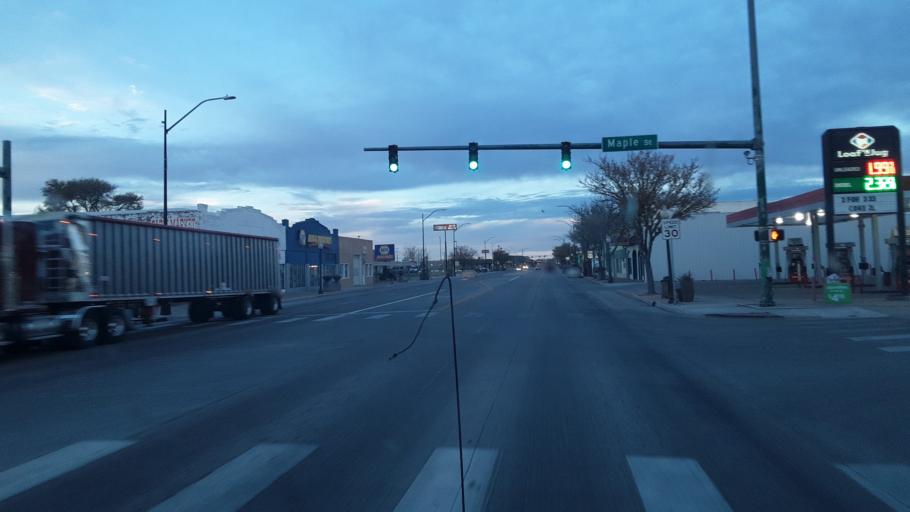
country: US
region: Colorado
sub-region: Prowers County
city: Lamar
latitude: 38.0922
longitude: -102.6194
